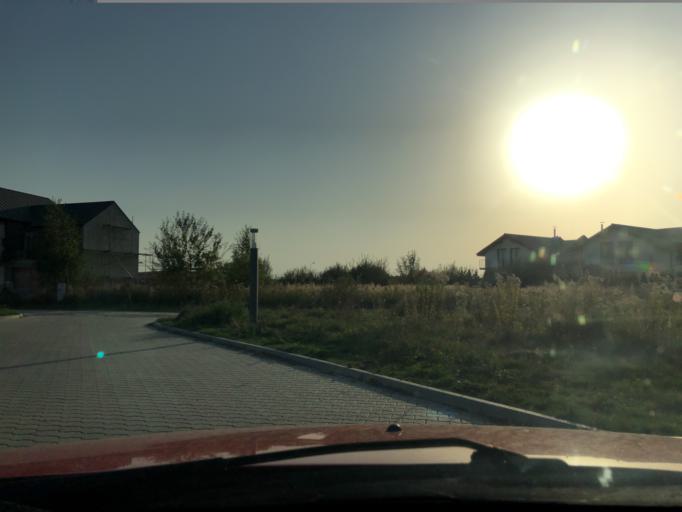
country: PL
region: Greater Poland Voivodeship
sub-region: Powiat poznanski
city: Dopiewo
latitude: 52.3768
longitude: 16.7356
